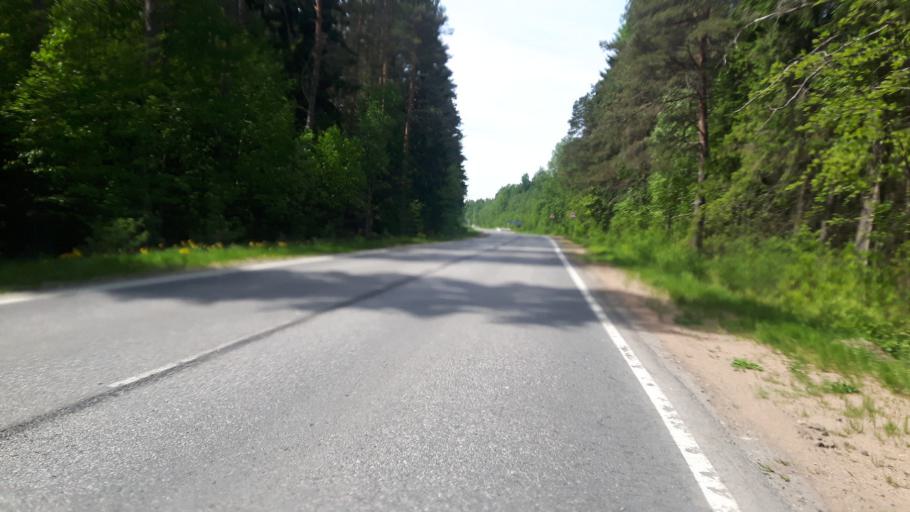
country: RU
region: Leningrad
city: Ust'-Luga
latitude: 59.6463
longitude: 28.2137
